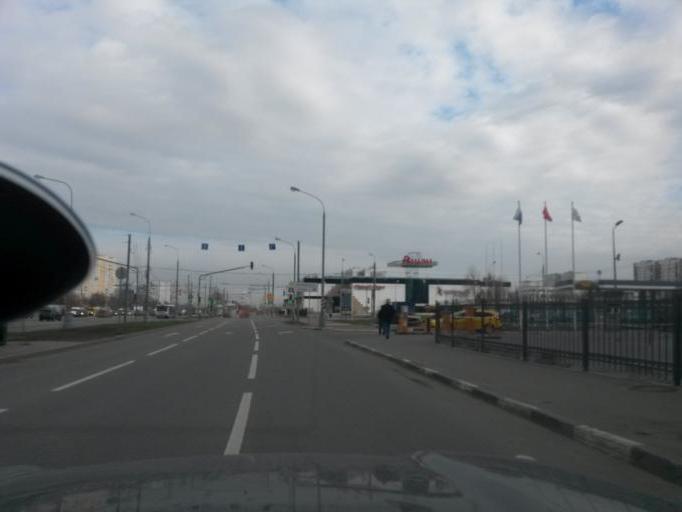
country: RU
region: Moscow
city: Orekhovo-Borisovo
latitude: 55.6186
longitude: 37.7141
